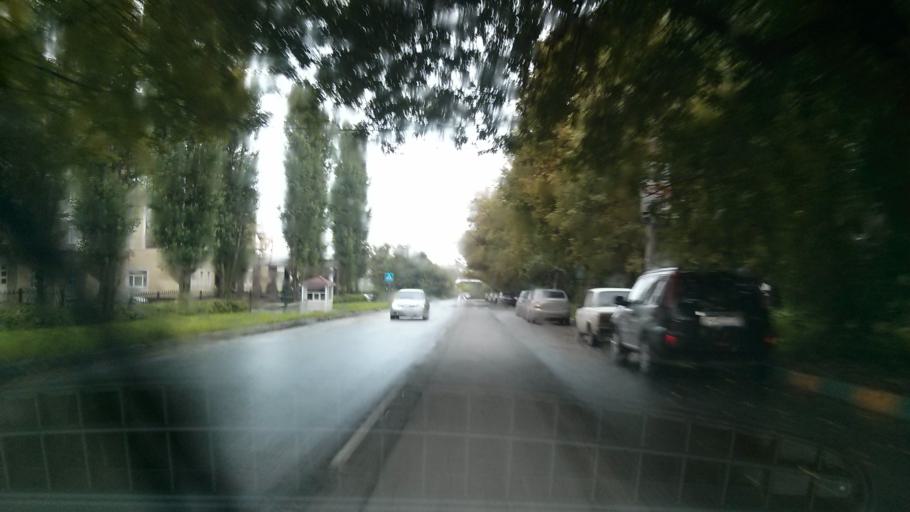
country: RU
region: Nizjnij Novgorod
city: Bor
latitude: 56.3176
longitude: 44.0551
